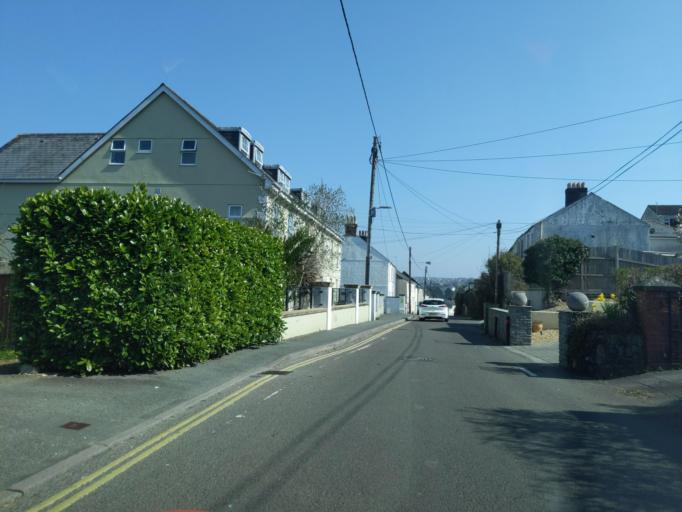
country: GB
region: England
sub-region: Devon
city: Plympton
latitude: 50.3853
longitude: -4.0642
